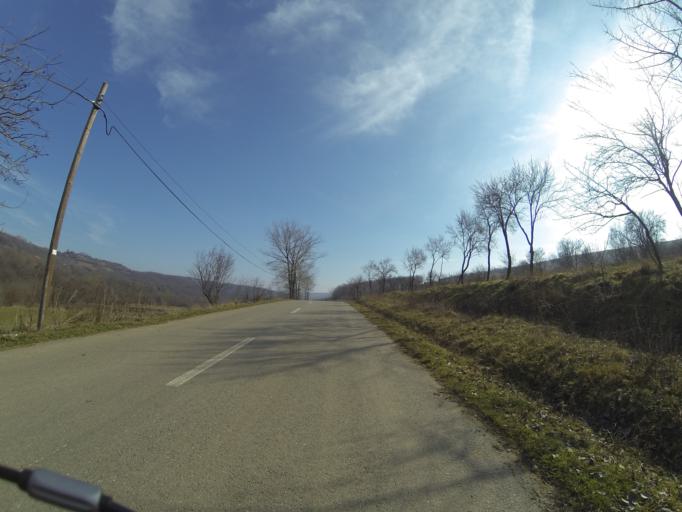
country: RO
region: Mehedinti
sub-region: Comuna Poroina Mare
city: Poroina Mare
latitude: 44.4946
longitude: 22.9284
